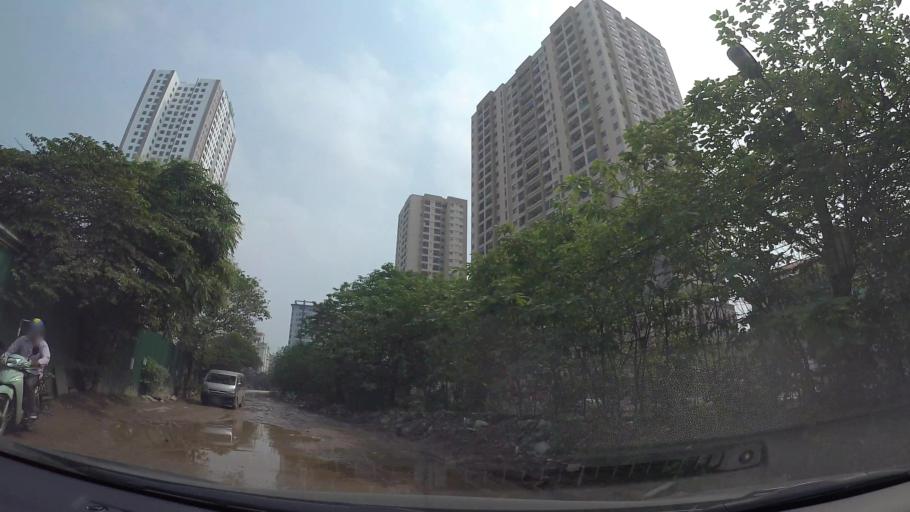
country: VN
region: Ha Noi
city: Van Dien
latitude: 20.9800
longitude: 105.8357
